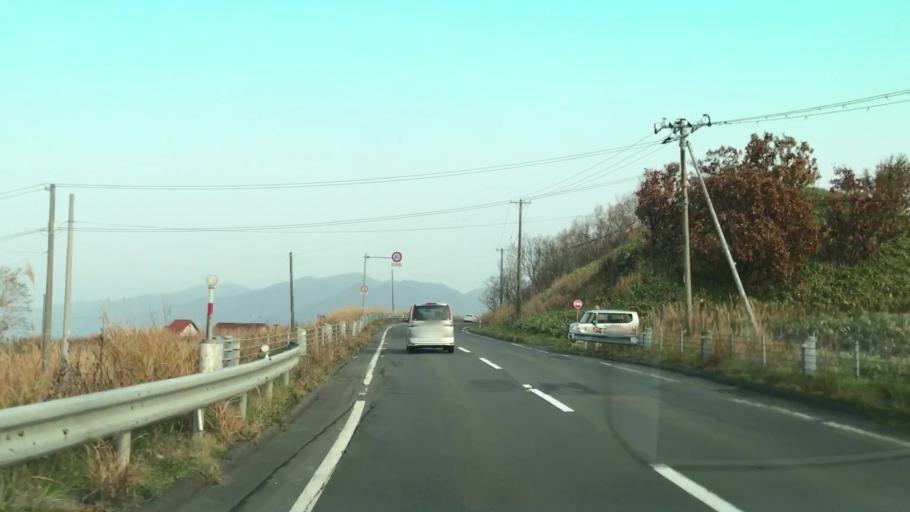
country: JP
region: Hokkaido
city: Ishikari
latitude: 43.3817
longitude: 141.4303
